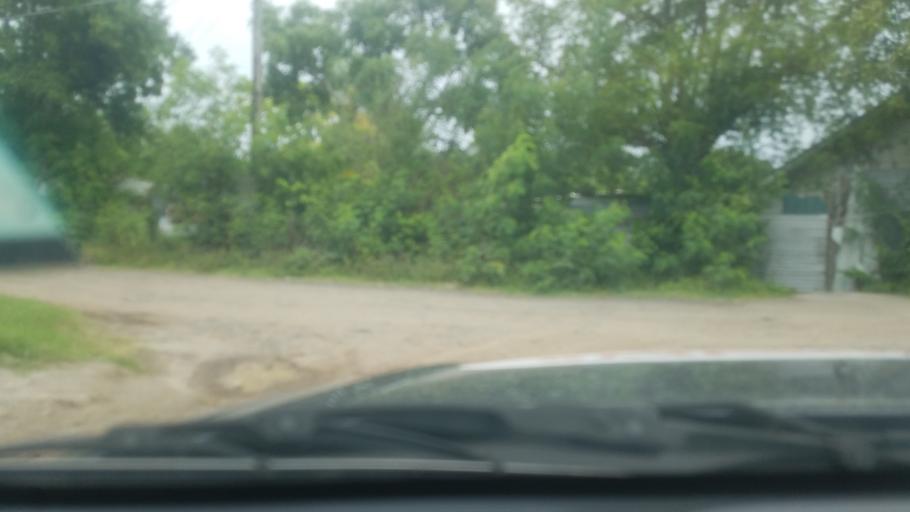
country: LC
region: Laborie Quarter
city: Laborie
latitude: 13.7494
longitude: -60.9789
